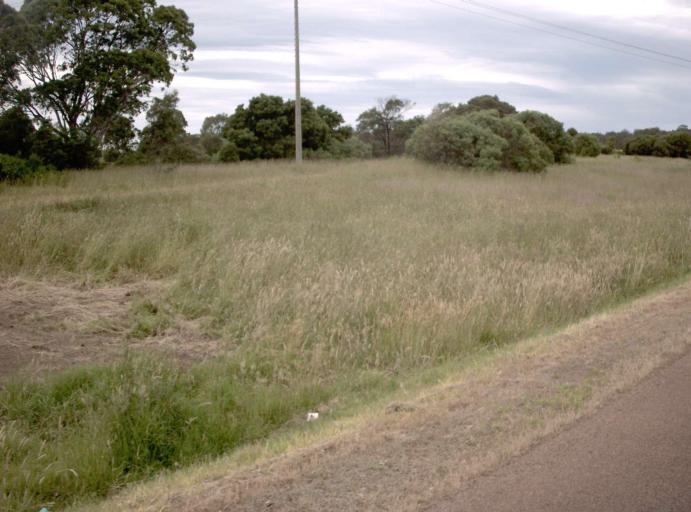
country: AU
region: Victoria
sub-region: East Gippsland
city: Bairnsdale
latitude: -37.8813
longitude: 147.6569
